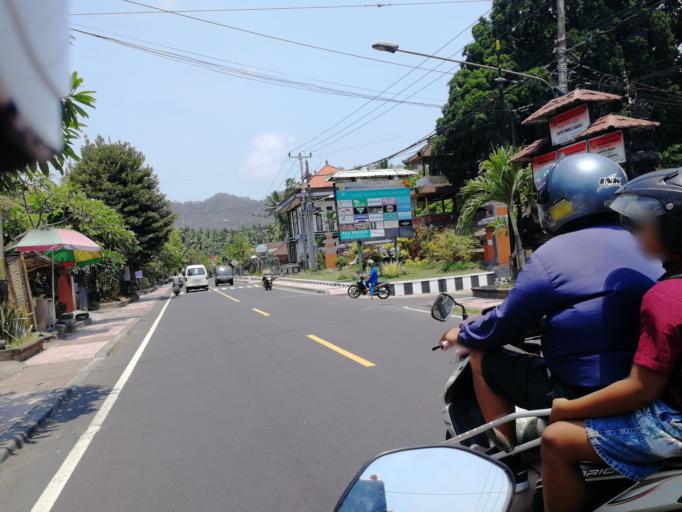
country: ID
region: Bali
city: Banjar Pegeringsingan
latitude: -8.4995
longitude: 115.5532
